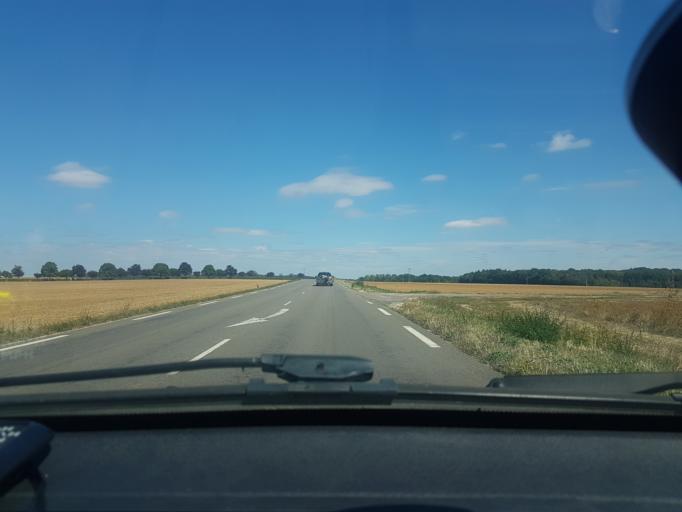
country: FR
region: Bourgogne
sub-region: Departement de la Cote-d'Or
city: Arc-sur-Tille
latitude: 47.3550
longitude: 5.2085
